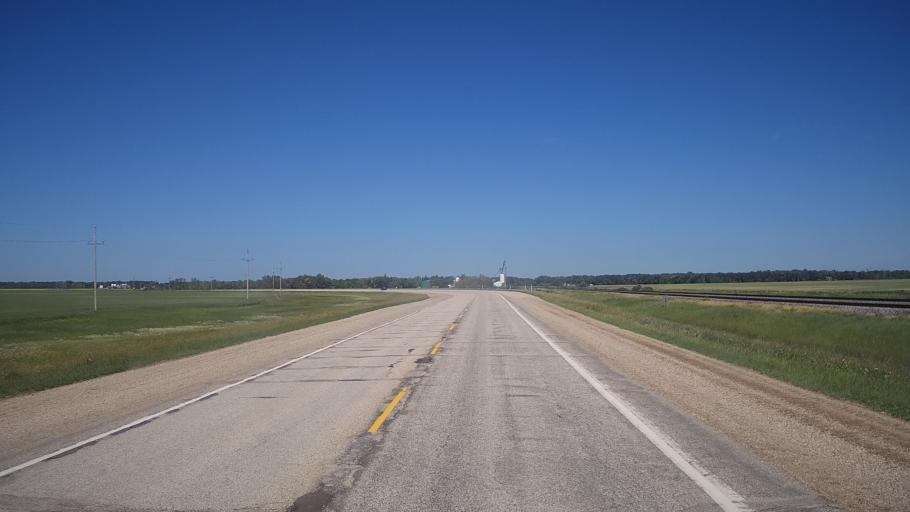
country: CA
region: Manitoba
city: Portage la Prairie
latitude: 50.1237
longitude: -98.5672
